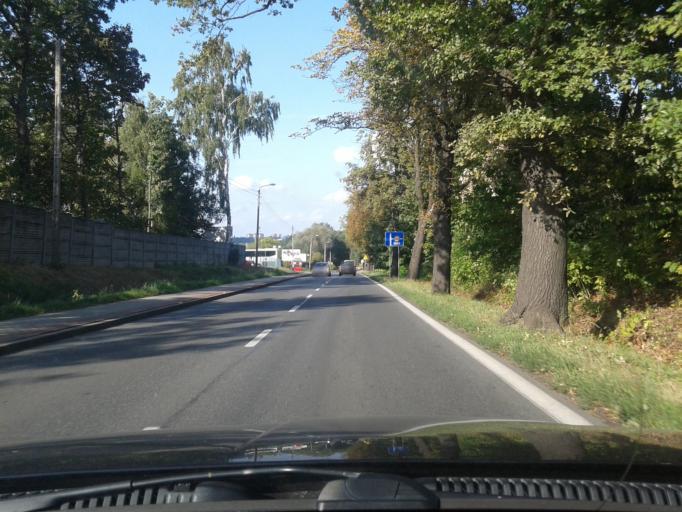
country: PL
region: Silesian Voivodeship
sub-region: Powiat wodzislawski
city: Turza Slaska
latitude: 49.9837
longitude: 18.4532
